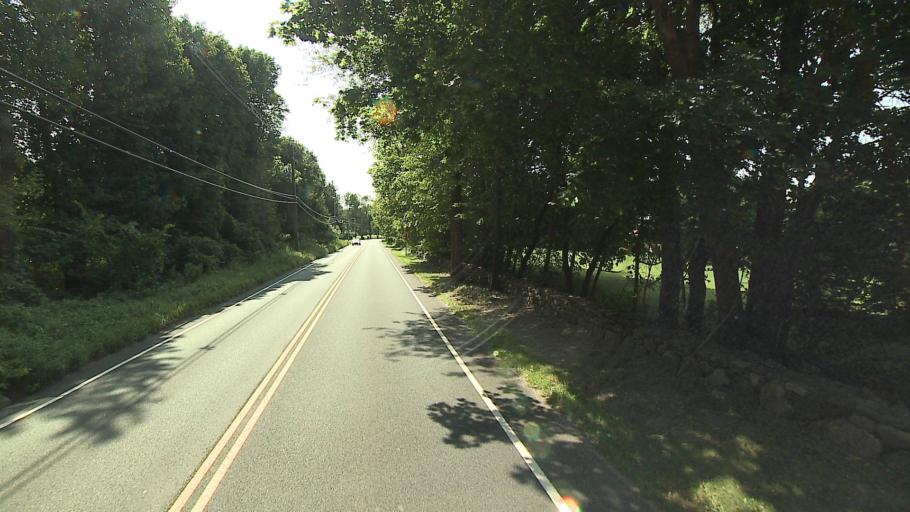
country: US
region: Connecticut
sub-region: Fairfield County
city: Newtown
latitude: 41.4504
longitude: -73.3777
